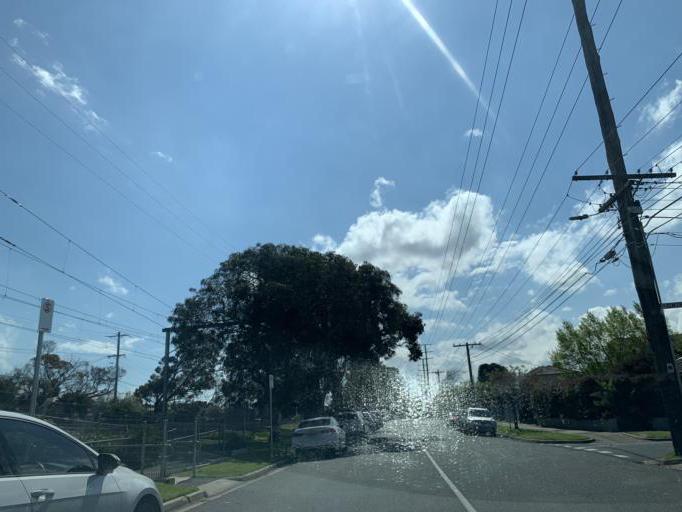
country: AU
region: Victoria
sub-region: Kingston
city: Mordialloc
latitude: -37.9956
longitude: 145.0794
